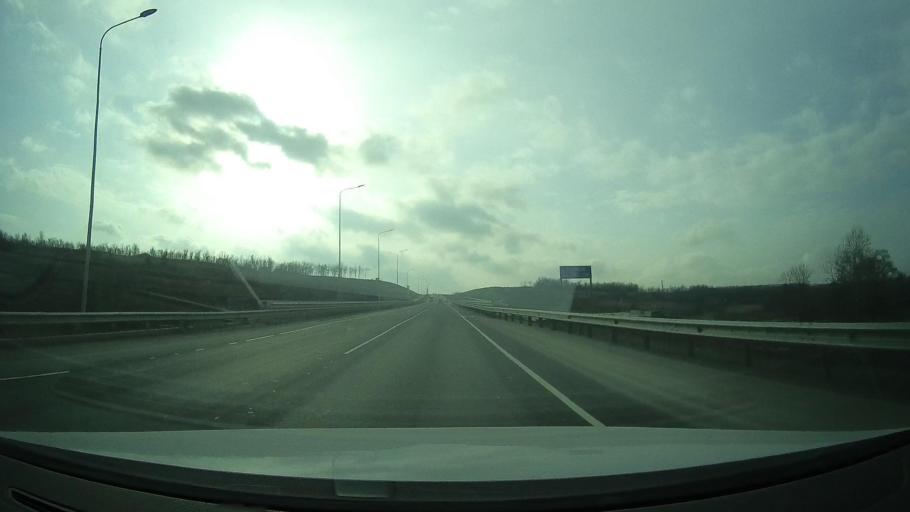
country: RU
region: Rostov
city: Grushevskaya
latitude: 47.4364
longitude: 39.8711
